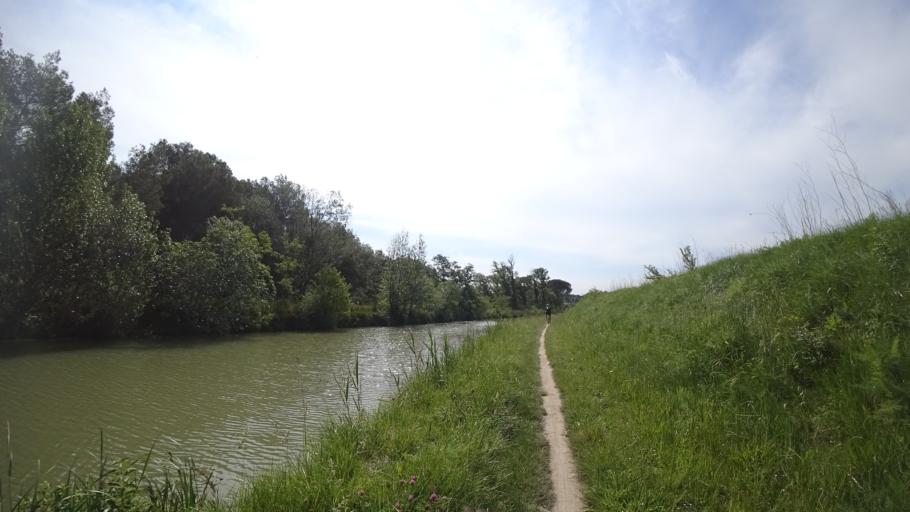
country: FR
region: Languedoc-Roussillon
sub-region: Departement de l'Herault
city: Olonzac
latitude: 43.2478
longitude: 2.7606
